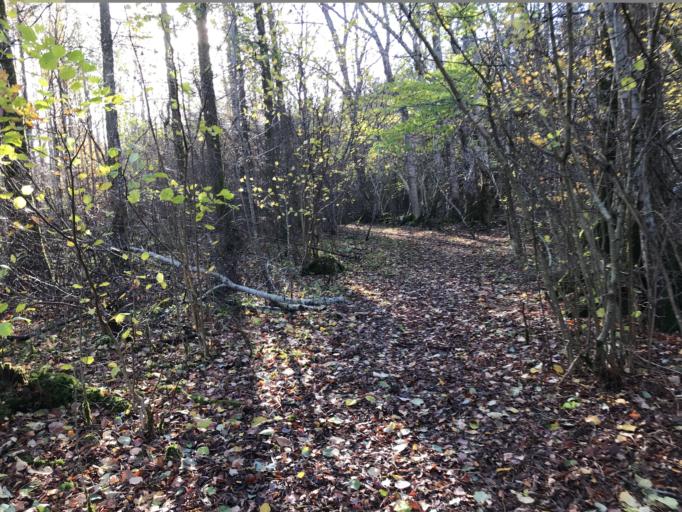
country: SE
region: Skane
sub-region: Svalovs Kommun
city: Kagerod
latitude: 56.0277
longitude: 13.1021
